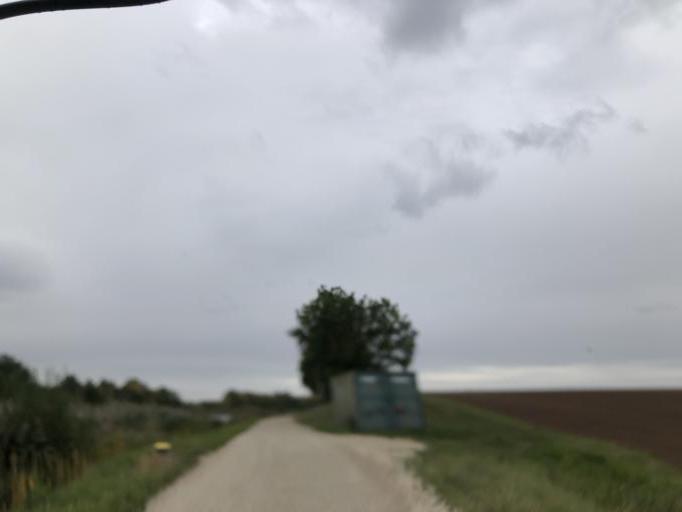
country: DE
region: Bavaria
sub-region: Regierungsbezirk Mittelfranken
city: Obermichelbach
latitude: 49.5387
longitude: 10.9678
